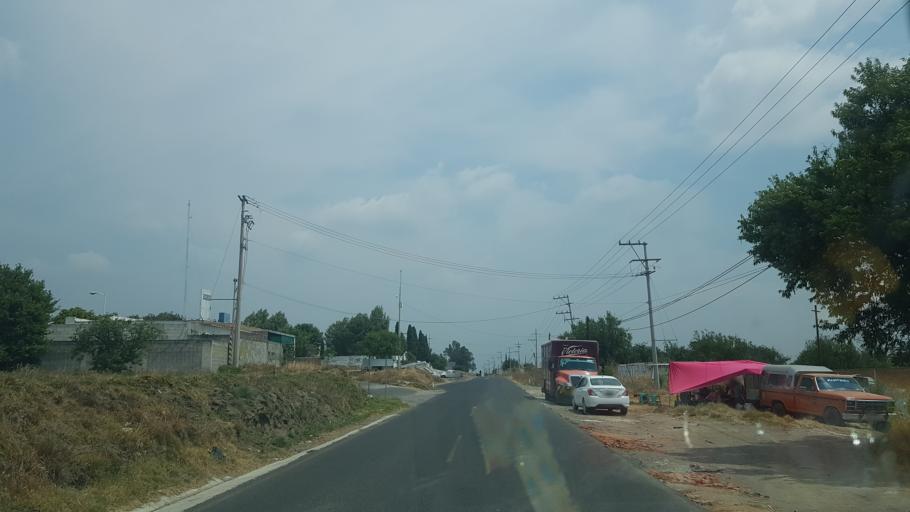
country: MX
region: Puebla
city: Huejotzingo
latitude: 19.1373
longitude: -98.4138
